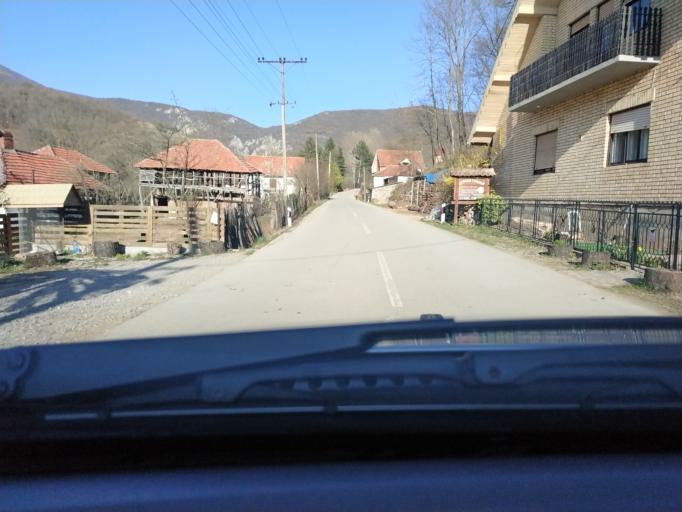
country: RS
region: Central Serbia
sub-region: Zajecarski Okrug
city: Soko Banja
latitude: 43.5554
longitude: 21.8214
